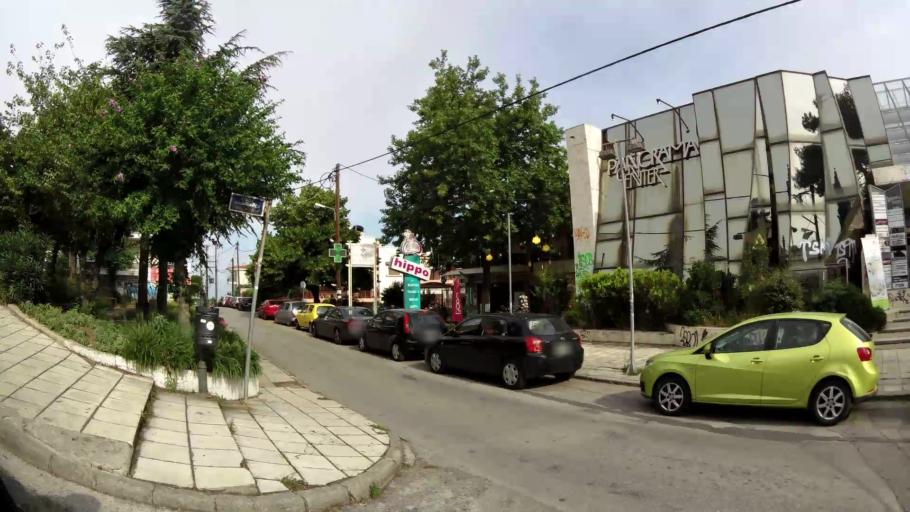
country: GR
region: Central Macedonia
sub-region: Nomos Thessalonikis
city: Panorama
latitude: 40.5909
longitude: 23.0328
